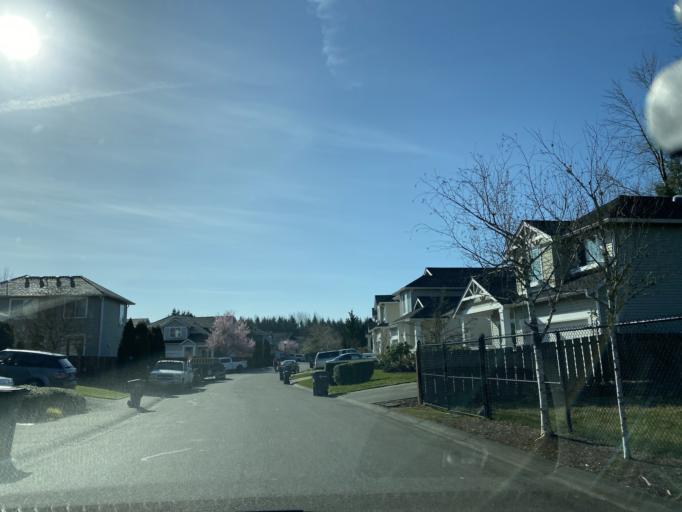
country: US
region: Washington
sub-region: King County
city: Ravensdale
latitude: 47.3550
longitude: -122.0155
